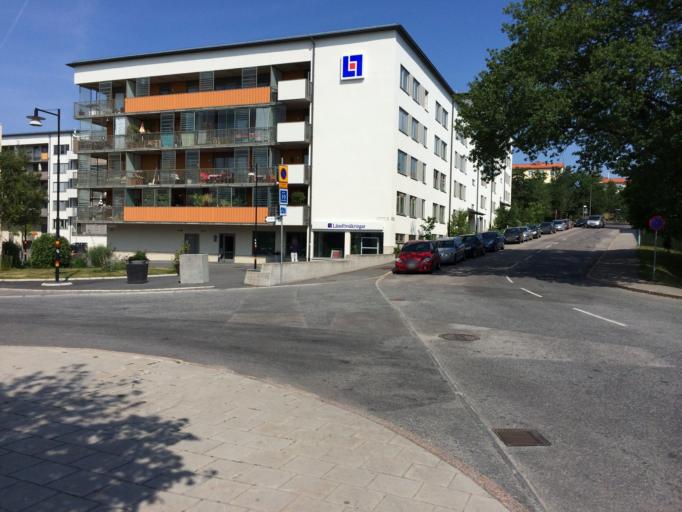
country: SE
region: Stockholm
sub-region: Stockholms Kommun
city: Arsta
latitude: 59.3001
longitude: 17.9954
